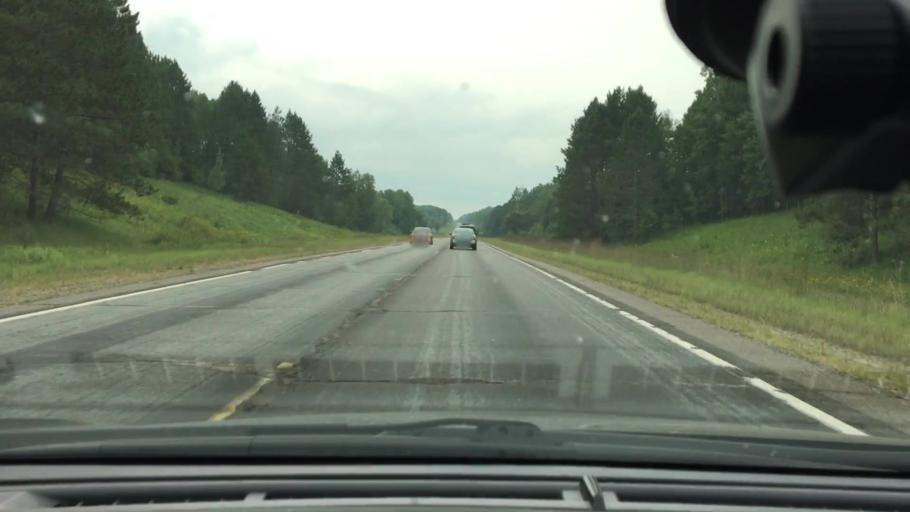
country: US
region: Minnesota
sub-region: Crow Wing County
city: Cross Lake
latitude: 46.6545
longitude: -93.9552
